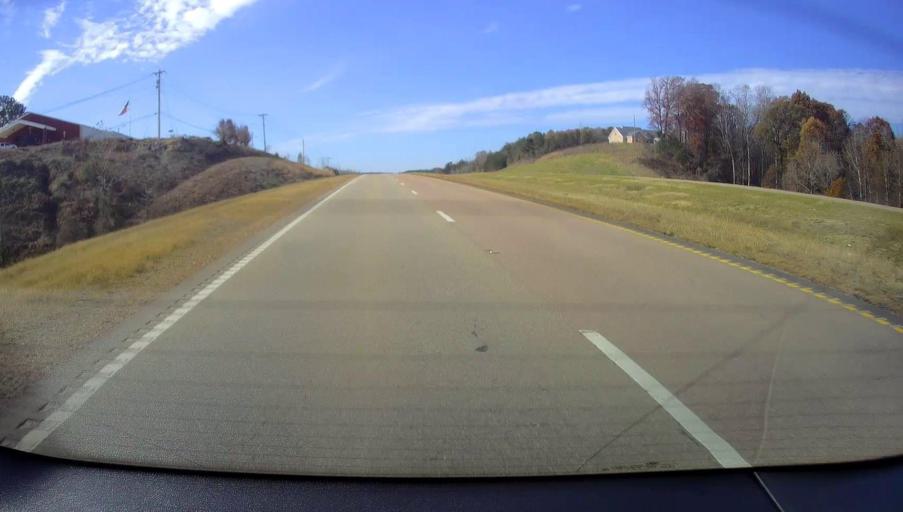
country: US
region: Mississippi
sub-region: Tippah County
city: Ripley
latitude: 34.9502
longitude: -88.9192
